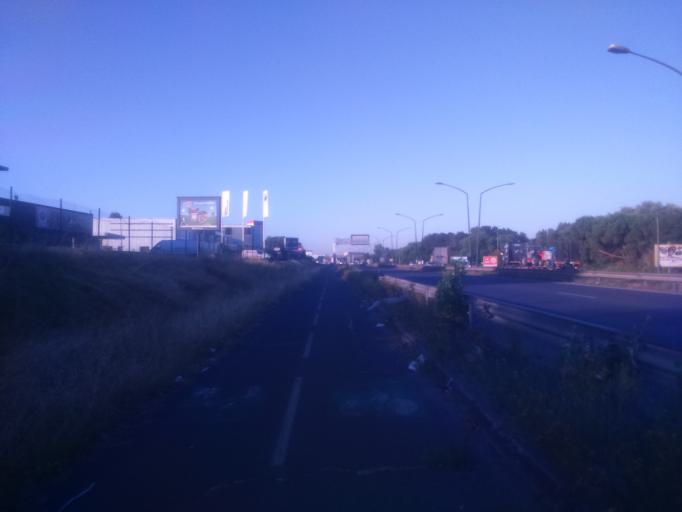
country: FR
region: Aquitaine
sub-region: Departement de la Gironde
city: Le Bouscat
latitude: 44.8750
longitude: -0.5645
